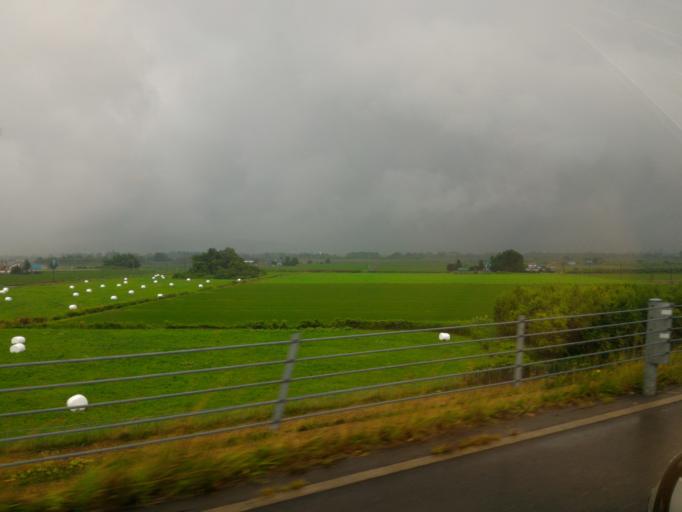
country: JP
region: Hokkaido
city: Nayoro
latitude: 44.3752
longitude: 142.4302
